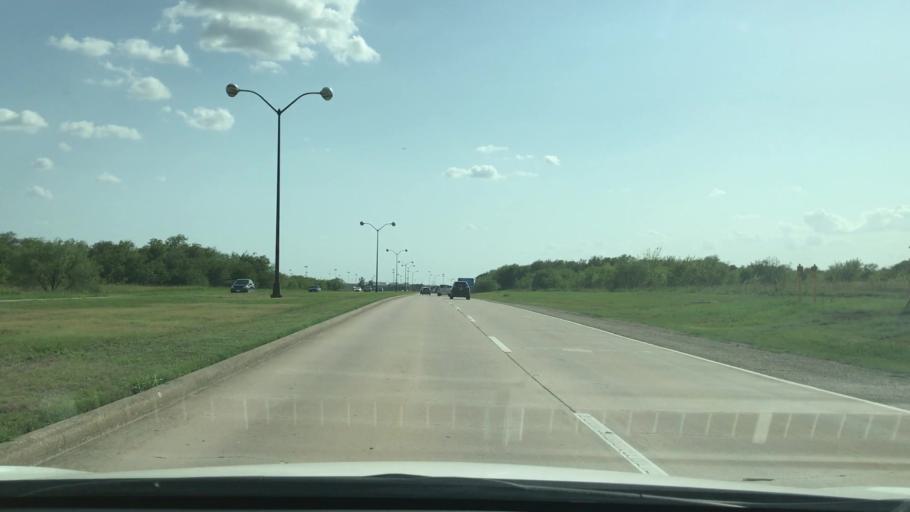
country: US
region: Texas
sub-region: Tarrant County
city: Euless
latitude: 32.8660
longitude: -97.0214
